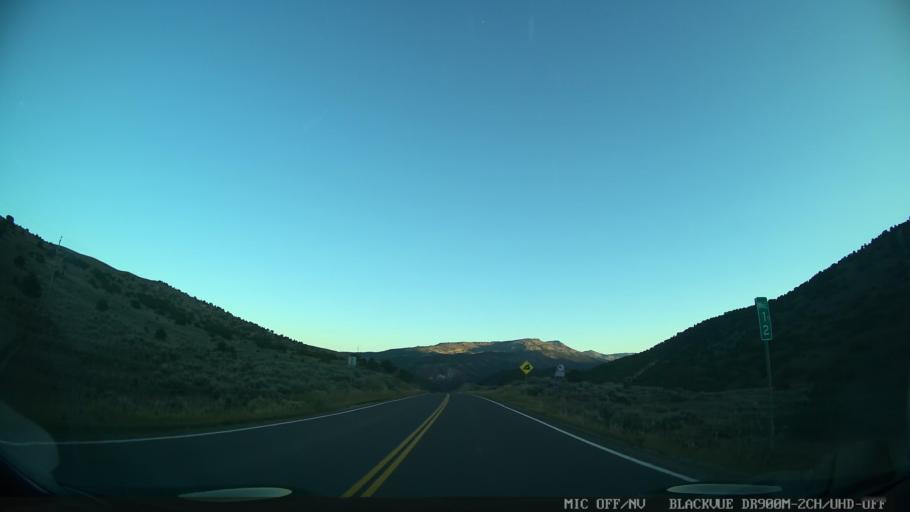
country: US
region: Colorado
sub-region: Eagle County
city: Edwards
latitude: 39.8355
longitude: -106.6380
